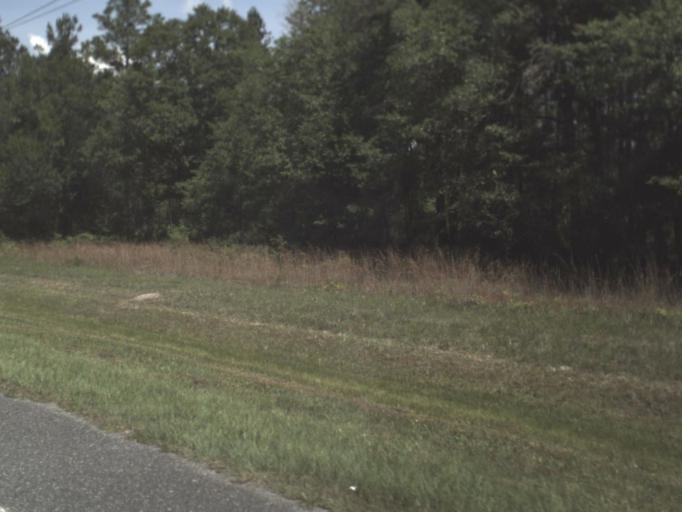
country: US
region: Florida
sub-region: Union County
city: Lake Butler
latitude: 29.9900
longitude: -82.2596
